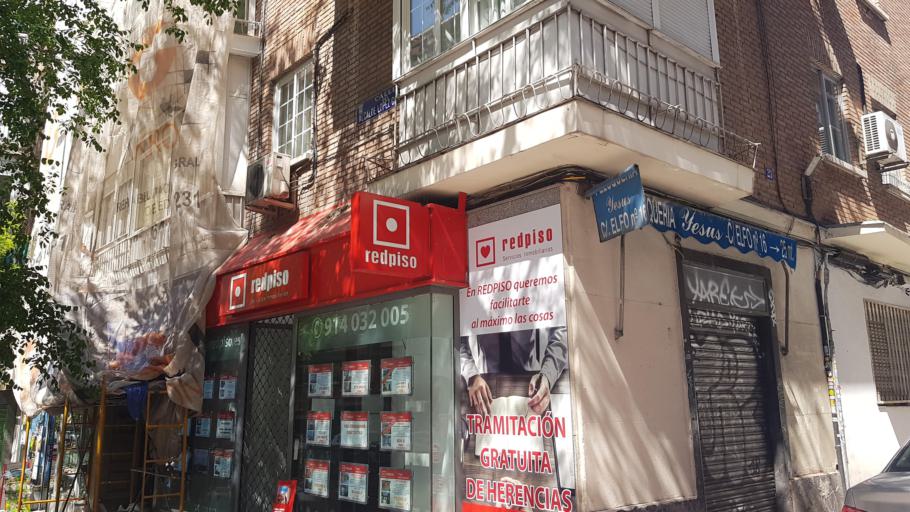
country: ES
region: Madrid
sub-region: Provincia de Madrid
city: Moratalaz
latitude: 40.4332
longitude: -3.6556
